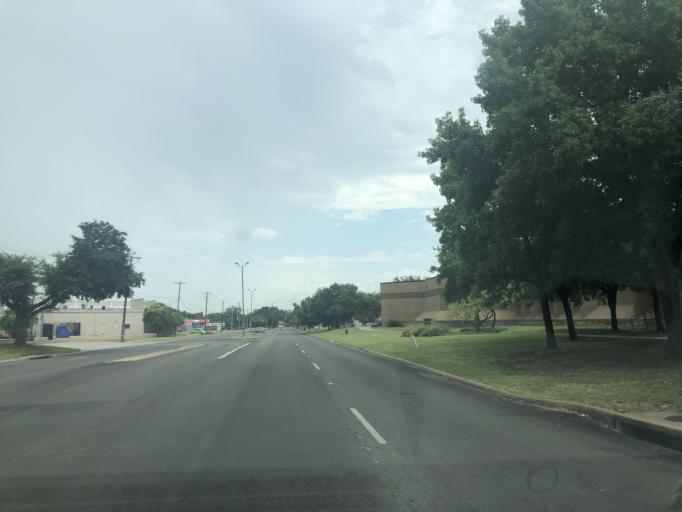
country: US
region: Texas
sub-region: Dallas County
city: Grand Prairie
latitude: 32.7380
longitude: -97.0181
